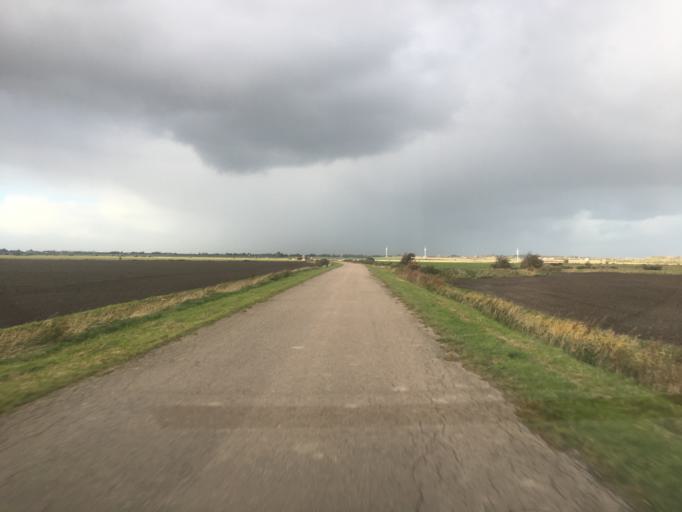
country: DE
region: Schleswig-Holstein
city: Aventoft
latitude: 54.9255
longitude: 8.7718
